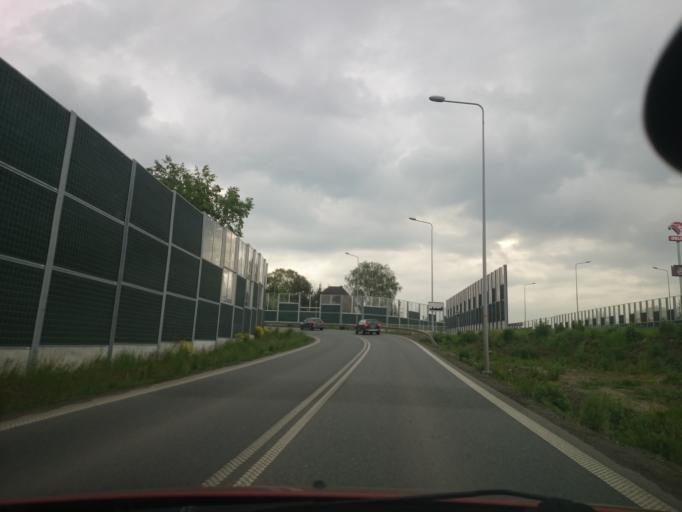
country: PL
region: Opole Voivodeship
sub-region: Powiat opolski
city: Czarnowasy
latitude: 50.7033
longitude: 17.9052
